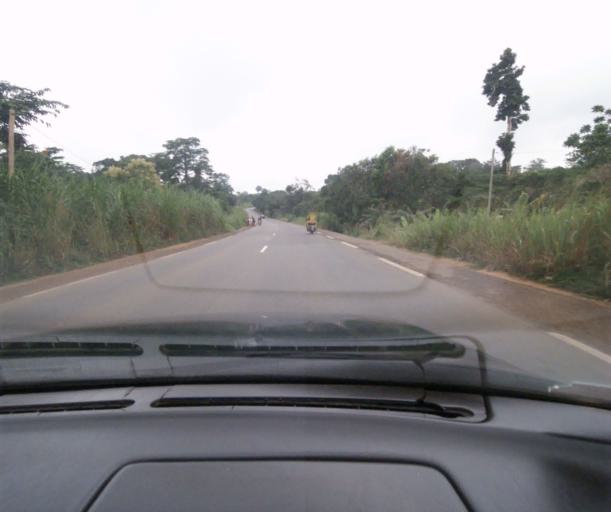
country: CM
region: Centre
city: Obala
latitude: 4.1660
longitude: 11.4923
